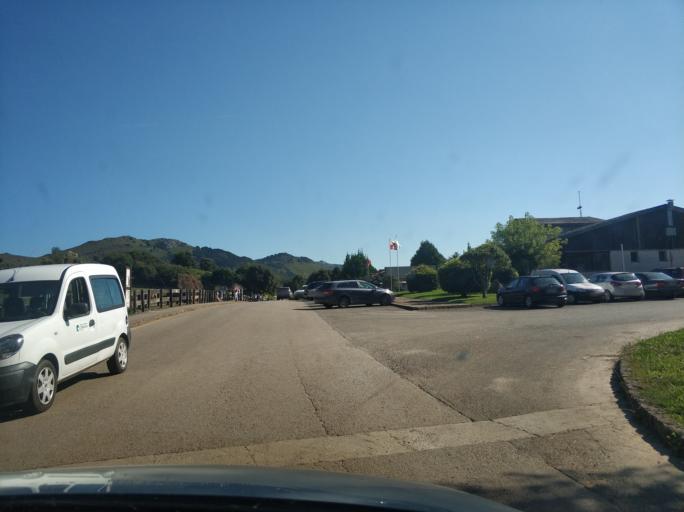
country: ES
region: Cantabria
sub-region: Provincia de Cantabria
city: Penagos
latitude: 43.3562
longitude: -3.8359
